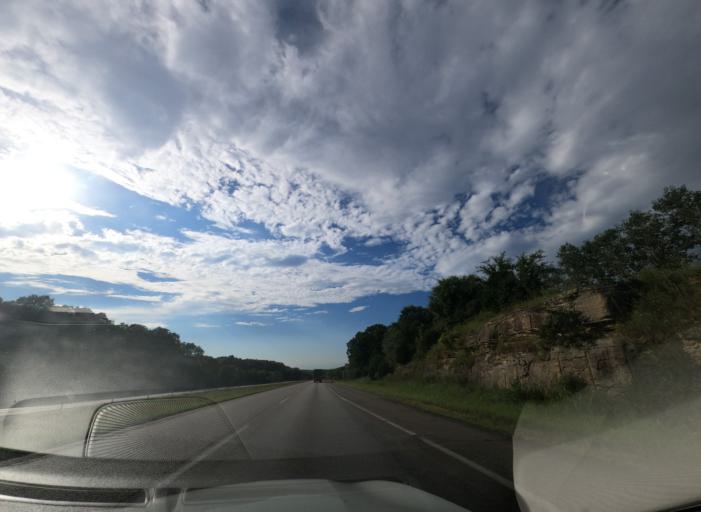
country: US
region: Missouri
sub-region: Sainte Genevieve County
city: Sainte Genevieve
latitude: 38.0337
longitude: -90.2537
